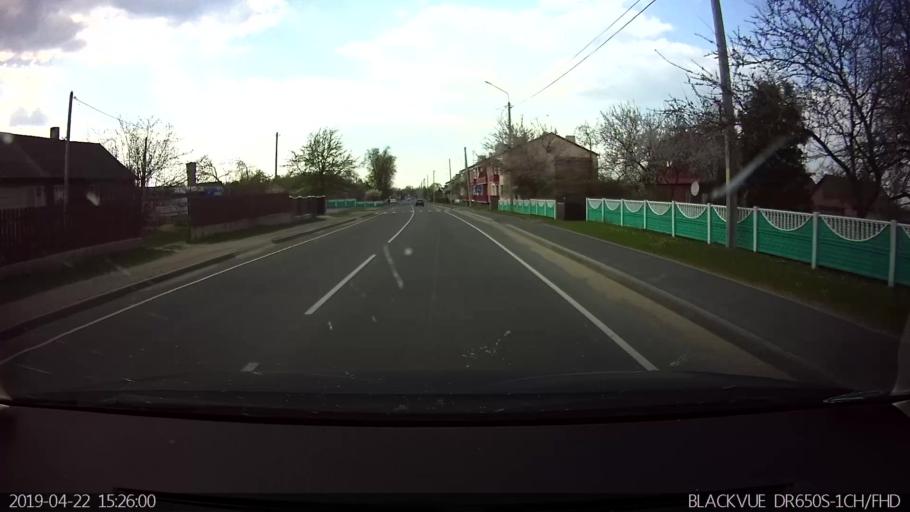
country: BY
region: Brest
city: Vysokaye
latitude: 52.3664
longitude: 23.3880
